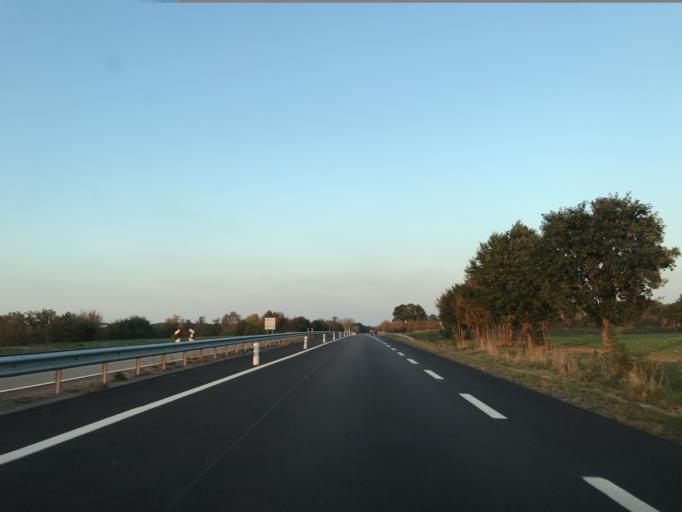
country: FR
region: Haute-Normandie
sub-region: Departement de l'Eure
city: Bourth
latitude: 48.6717
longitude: 0.7908
